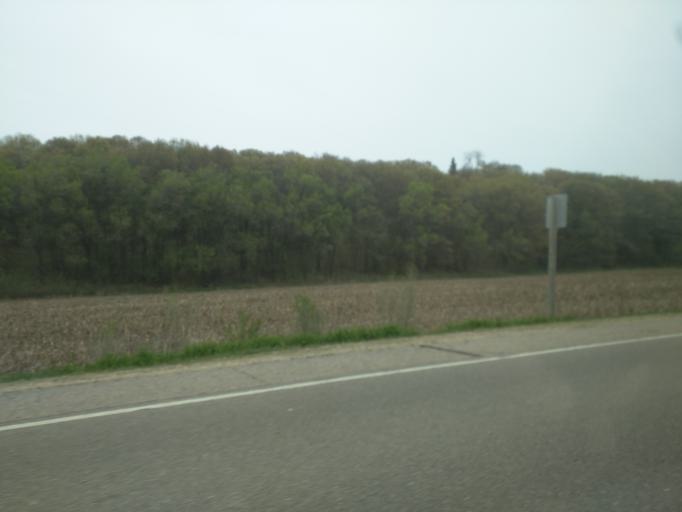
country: US
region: Minnesota
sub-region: Goodhue County
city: Red Wing
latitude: 44.5856
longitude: -92.4489
